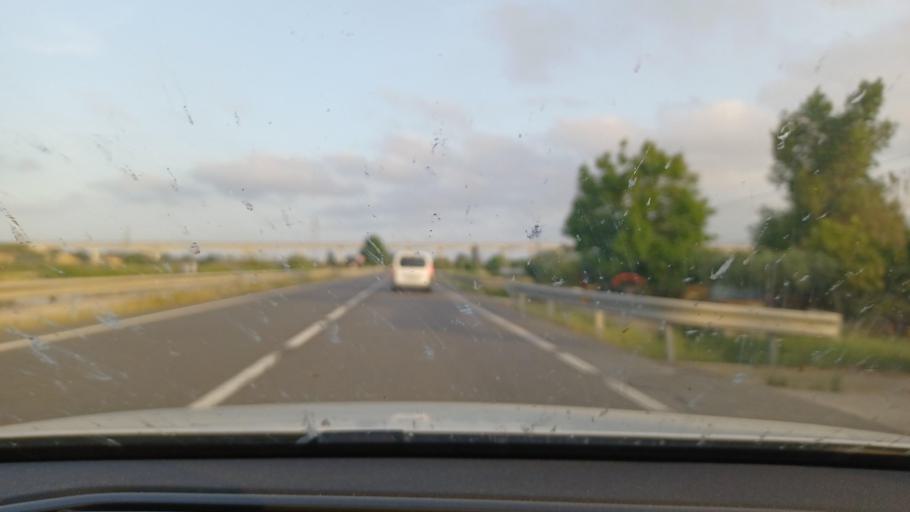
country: ES
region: Catalonia
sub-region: Provincia de Tarragona
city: Amposta
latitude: 40.7363
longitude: 0.5674
